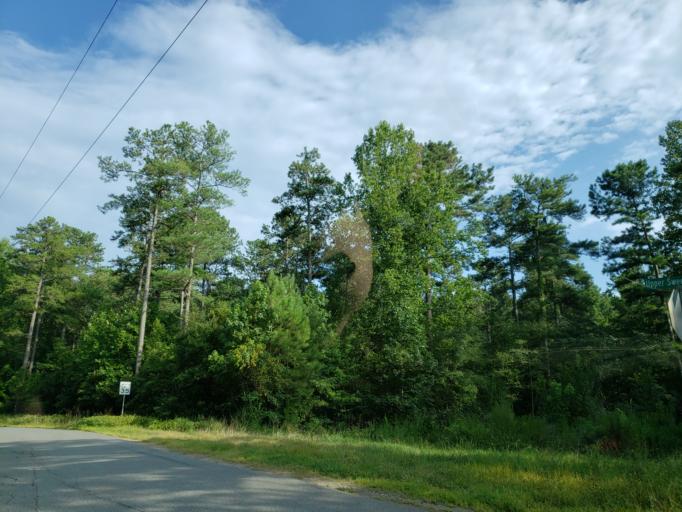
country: US
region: Georgia
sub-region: Bartow County
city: Emerson
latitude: 34.1909
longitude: -84.6570
